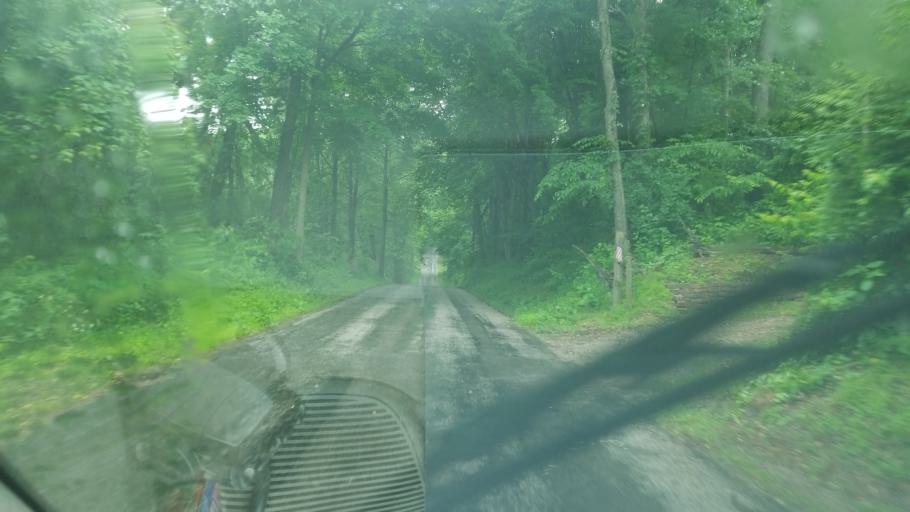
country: US
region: Ohio
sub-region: Sandusky County
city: Bellville
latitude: 40.6240
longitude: -82.4598
